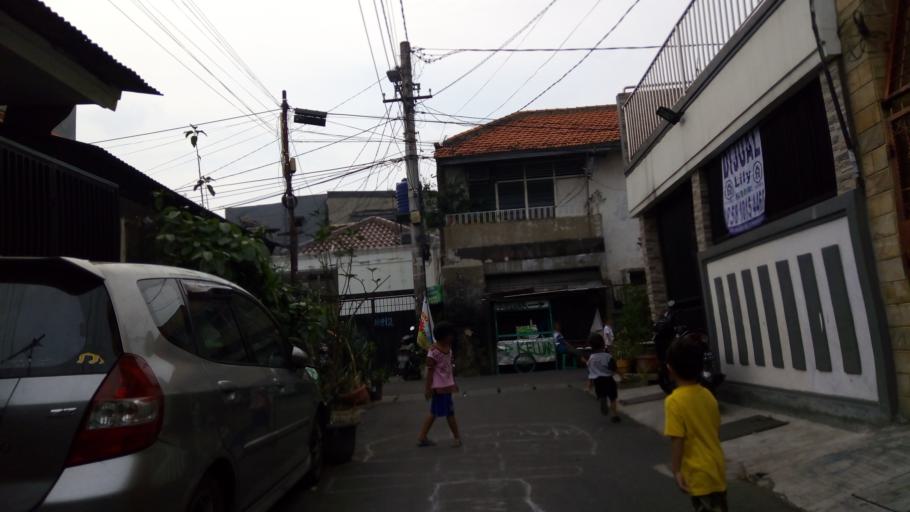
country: ID
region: Jakarta Raya
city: Jakarta
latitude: -6.1633
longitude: 106.8361
